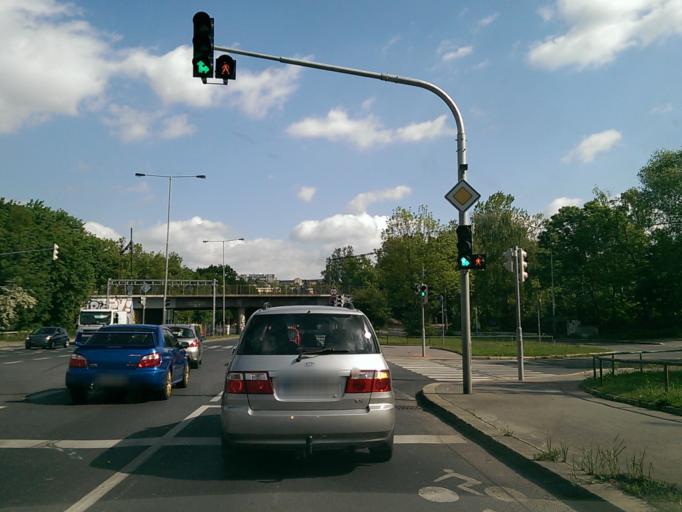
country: CZ
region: Praha
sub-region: Praha 4
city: Hodkovicky
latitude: 50.0345
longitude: 14.4558
